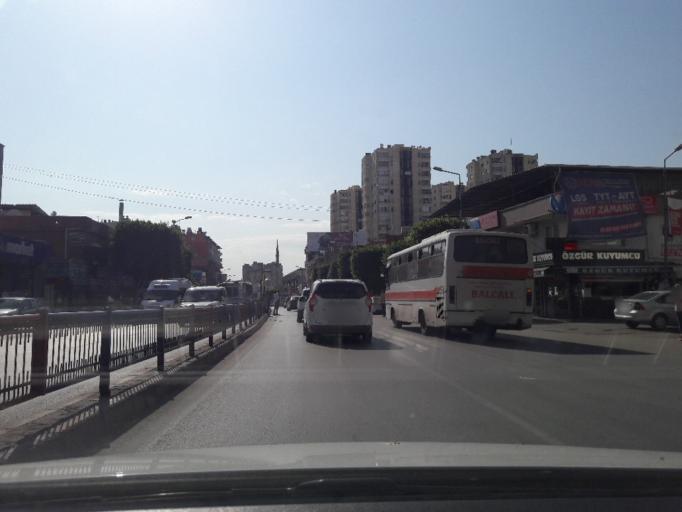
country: TR
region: Adana
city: Adana
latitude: 37.0146
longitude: 35.3223
